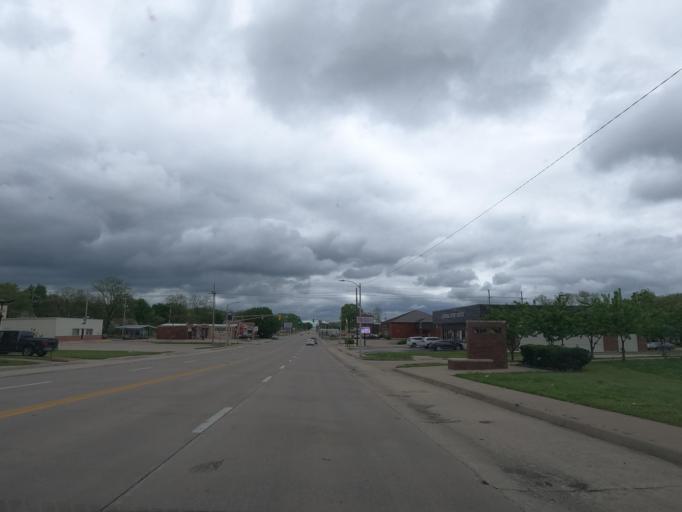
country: US
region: Kansas
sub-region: Labette County
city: Parsons
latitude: 37.3404
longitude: -95.2555
